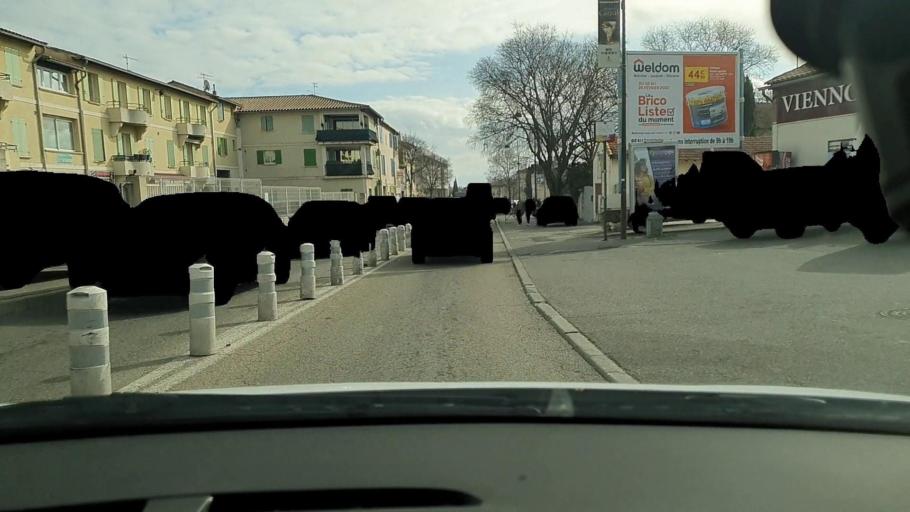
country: FR
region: Languedoc-Roussillon
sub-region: Departement du Gard
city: Beaucaire
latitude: 43.8112
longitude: 4.6357
